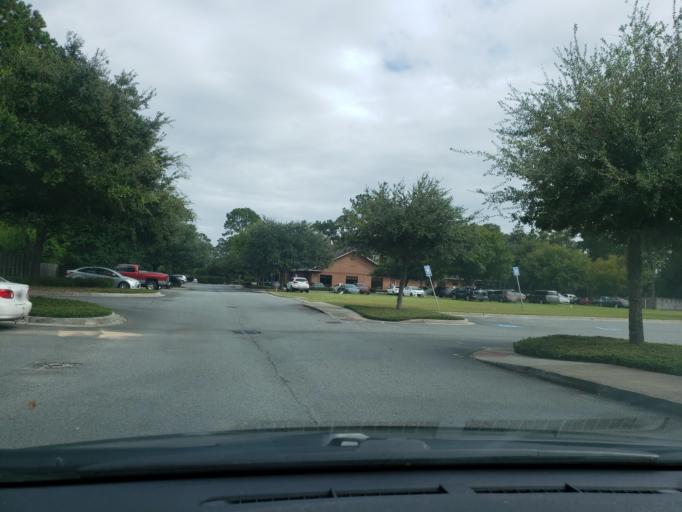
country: US
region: Georgia
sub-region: Chatham County
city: Isle of Hope
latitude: 32.0105
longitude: -81.0985
